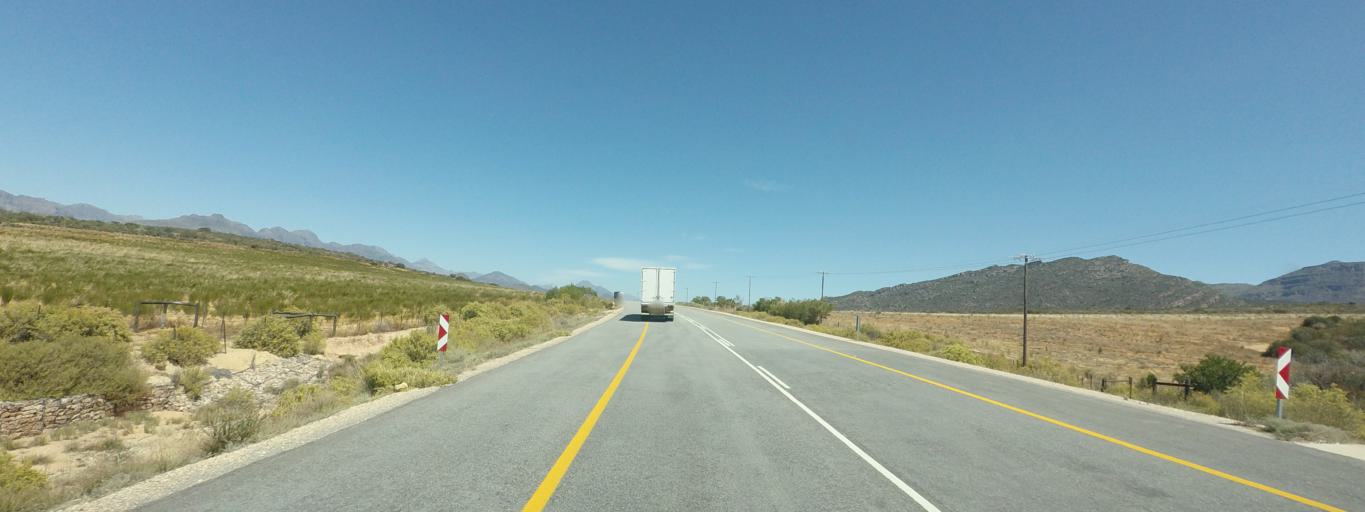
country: ZA
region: Western Cape
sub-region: West Coast District Municipality
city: Clanwilliam
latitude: -32.3175
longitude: 18.9127
